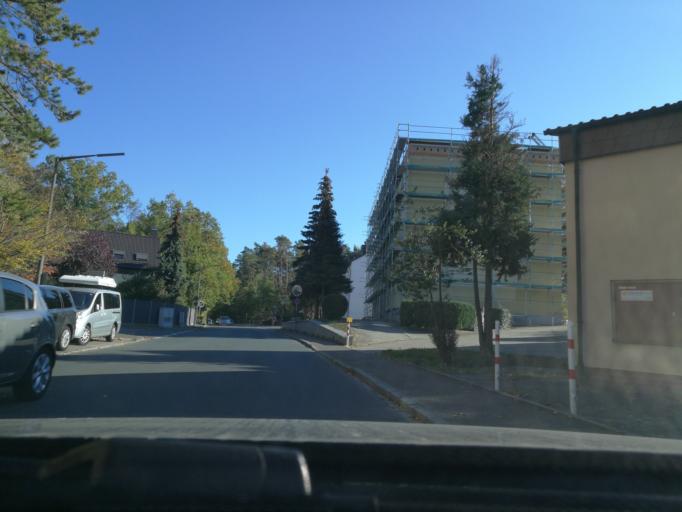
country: DE
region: Bavaria
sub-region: Regierungsbezirk Mittelfranken
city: Zirndorf
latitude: 49.4572
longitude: 10.9323
